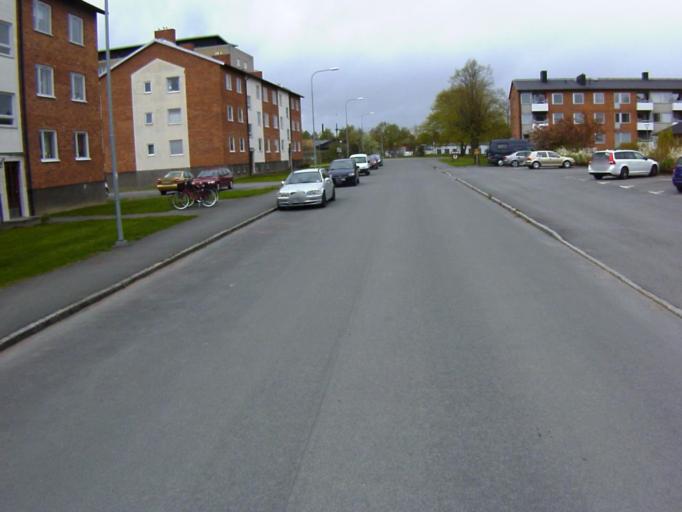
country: SE
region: Skane
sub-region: Kristianstads Kommun
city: Kristianstad
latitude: 56.0433
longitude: 14.1628
